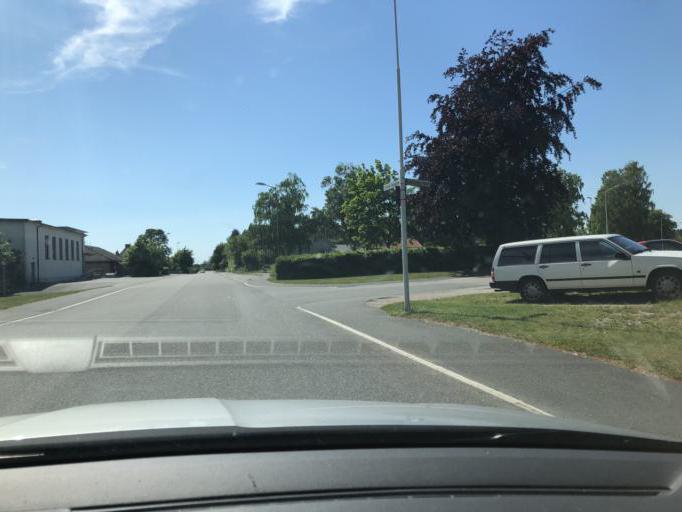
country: SE
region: Skane
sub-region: Bromolla Kommun
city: Bromoella
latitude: 56.0758
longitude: 14.4855
